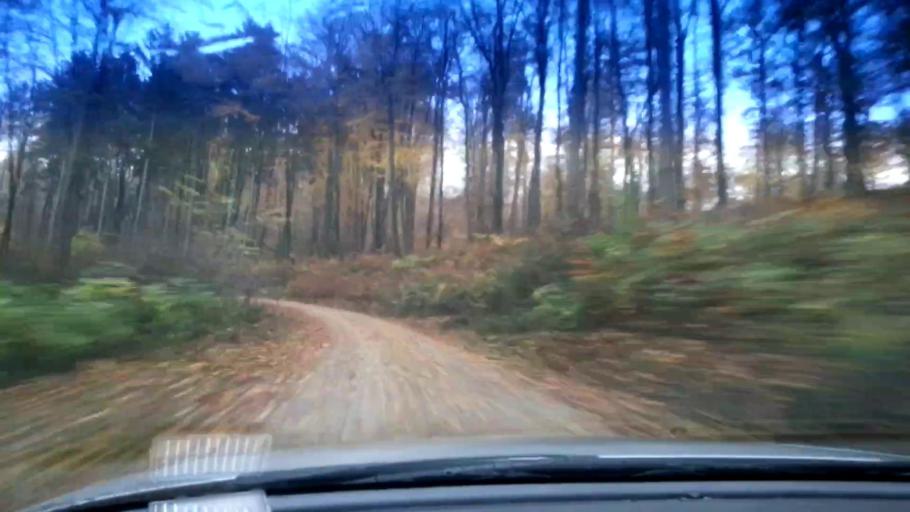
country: DE
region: Bavaria
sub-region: Upper Franconia
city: Litzendorf
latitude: 49.9406
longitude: 11.0278
